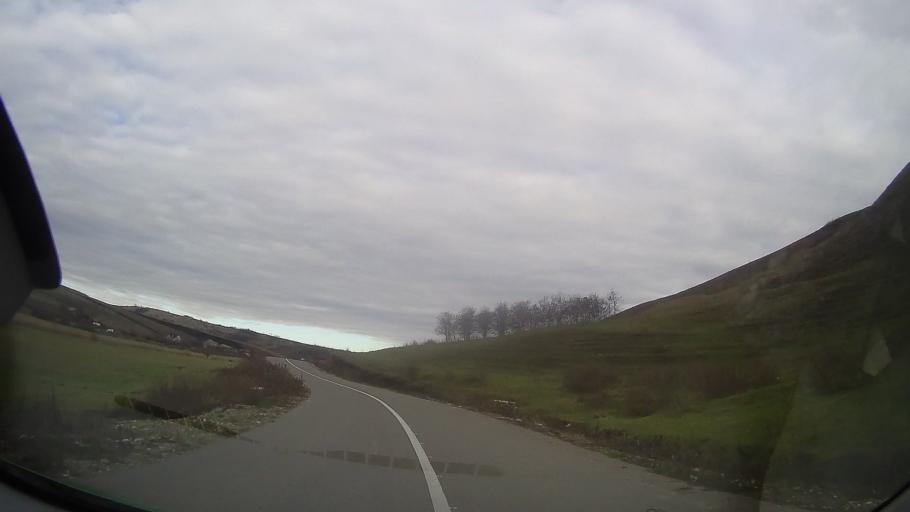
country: RO
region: Bistrita-Nasaud
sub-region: Comuna Silvasu de Campie
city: Silvasu de Campie
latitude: 46.7880
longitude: 24.2861
